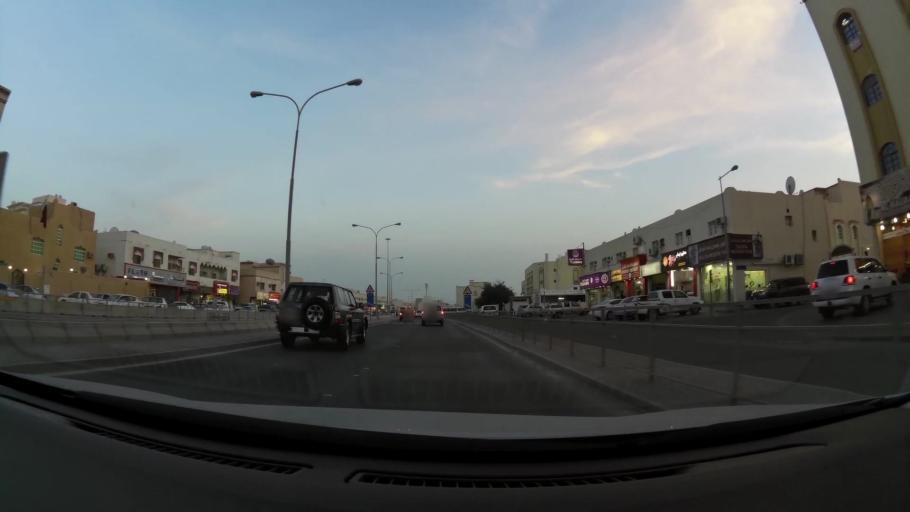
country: QA
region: Al Wakrah
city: Al Wakrah
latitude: 25.1625
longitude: 51.5979
